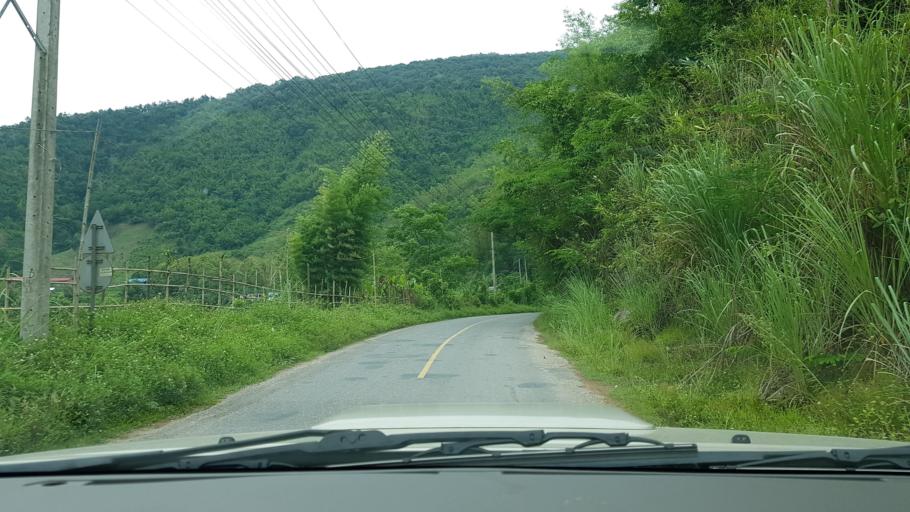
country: LA
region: Oudomxai
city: Muang La
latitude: 20.8734
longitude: 102.1393
